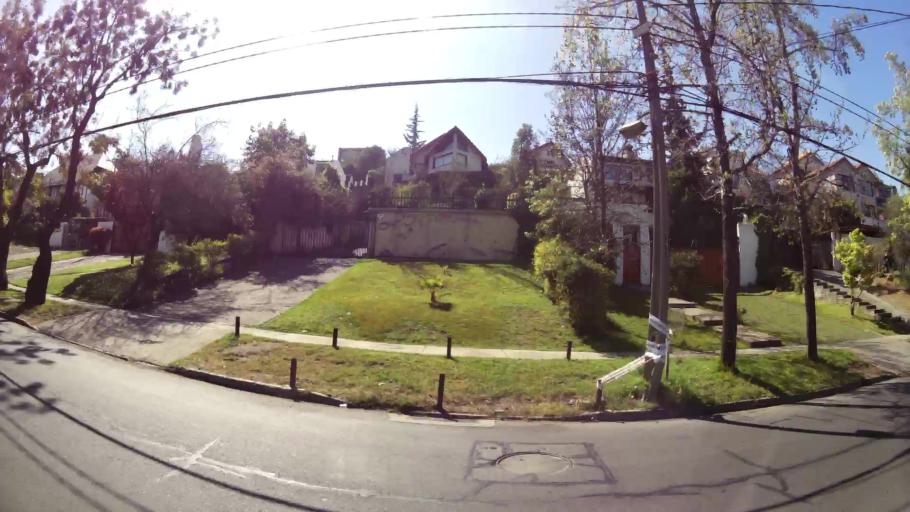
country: CL
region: Santiago Metropolitan
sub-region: Provincia de Santiago
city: Villa Presidente Frei, Nunoa, Santiago, Chile
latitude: -33.4109
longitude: -70.5359
